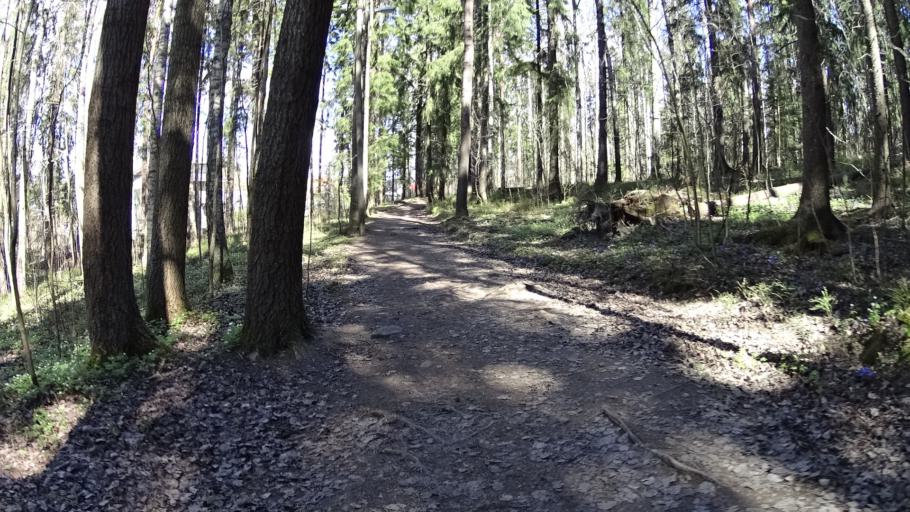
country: FI
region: Uusimaa
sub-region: Helsinki
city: Kilo
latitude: 60.2327
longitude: 24.7589
